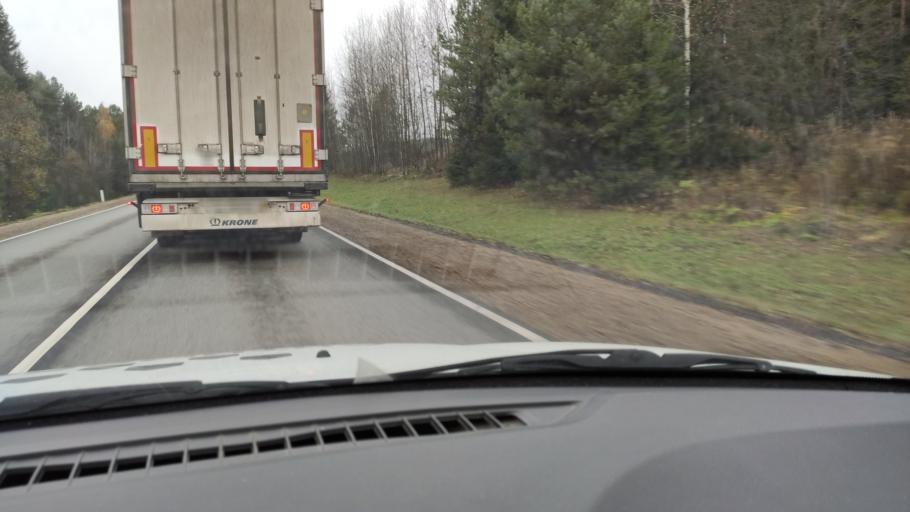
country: RU
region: Kirov
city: Slobodskoy
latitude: 58.7717
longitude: 50.3741
